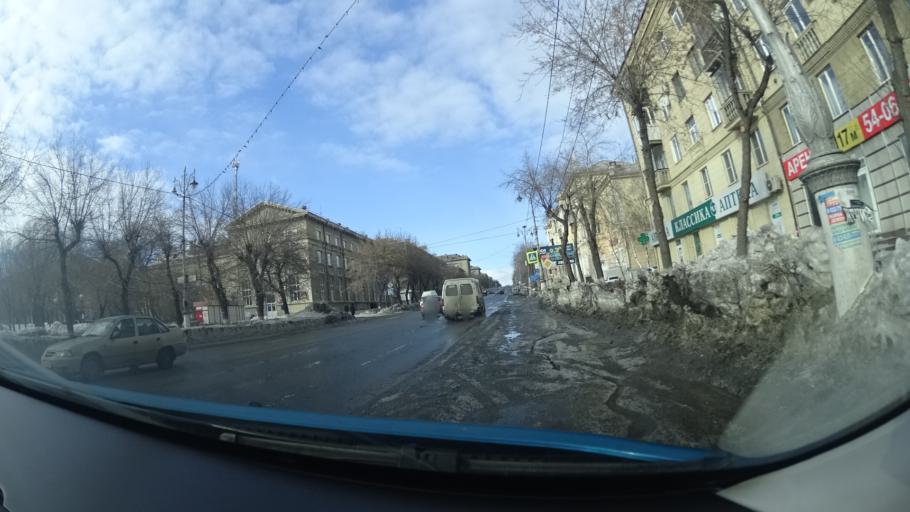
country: RU
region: Chelyabinsk
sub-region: Gorod Magnitogorsk
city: Magnitogorsk
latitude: 53.4241
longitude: 58.9838
